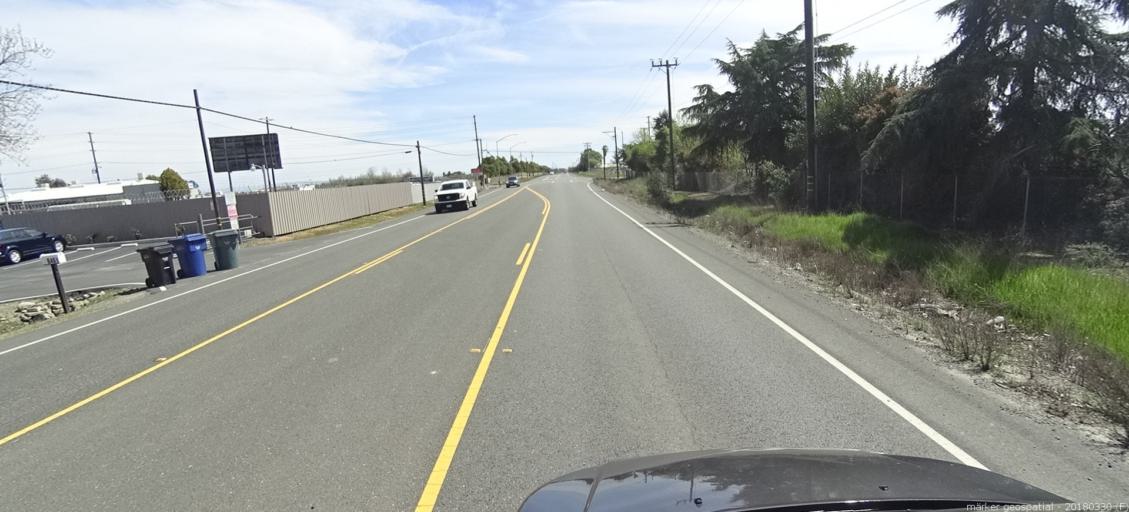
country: US
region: California
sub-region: Sacramento County
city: Rosemont
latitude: 38.5319
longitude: -121.3460
